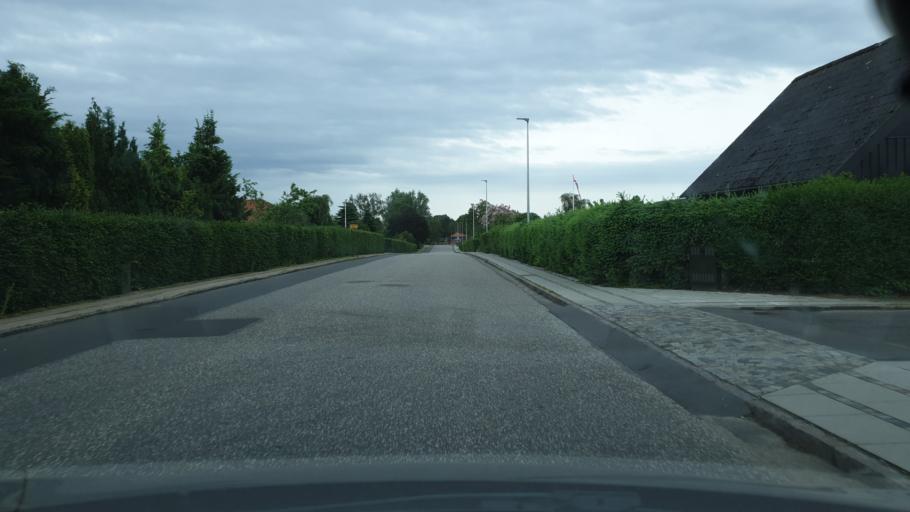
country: DK
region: South Denmark
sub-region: Kolding Kommune
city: Kolding
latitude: 55.5055
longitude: 9.4958
